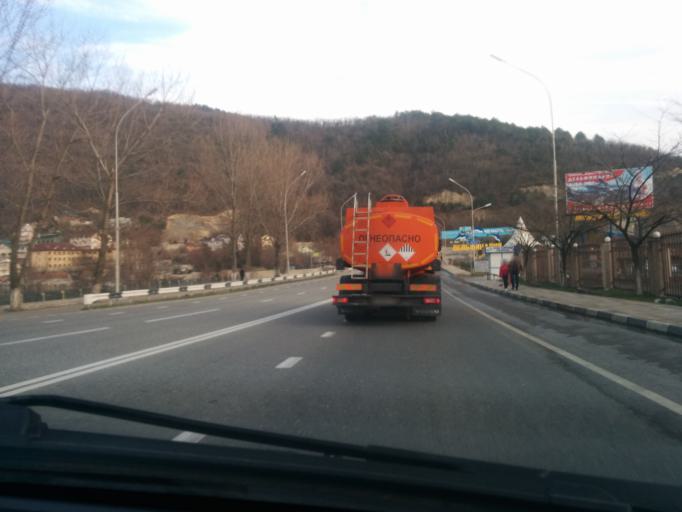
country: RU
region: Krasnodarskiy
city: Nebug
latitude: 44.1658
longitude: 38.9991
